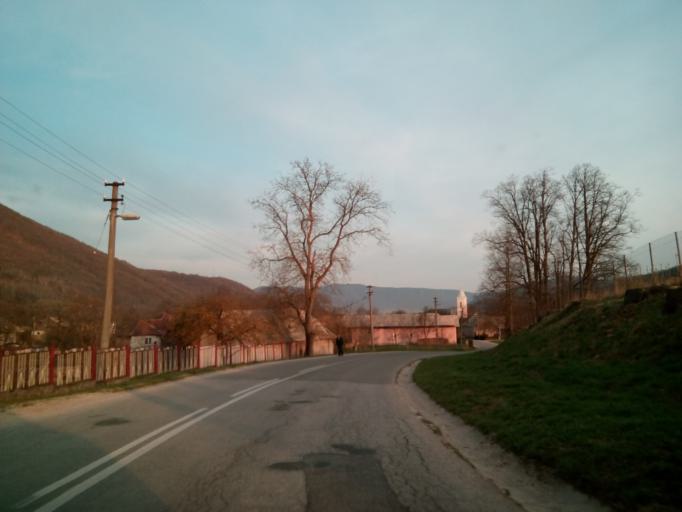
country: SK
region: Kosicky
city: Dobsina
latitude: 48.7051
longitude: 20.2959
